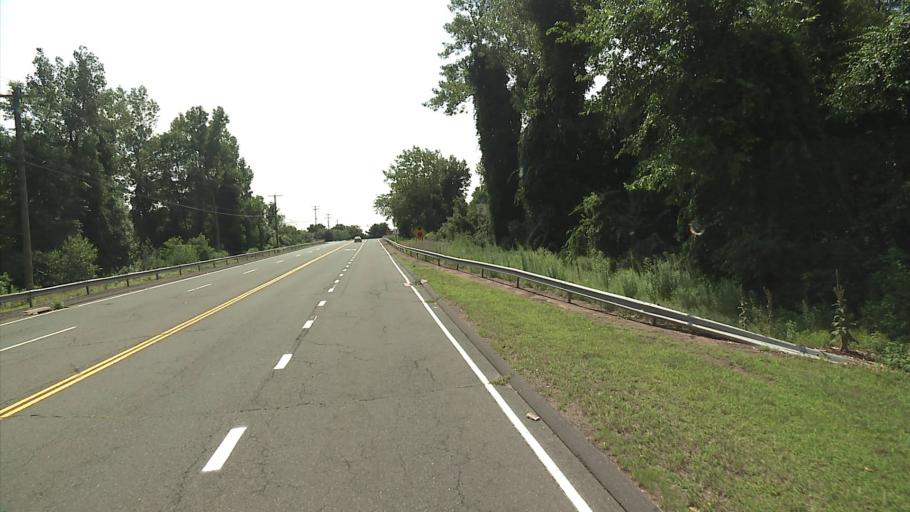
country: US
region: Connecticut
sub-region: Tolland County
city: Rockville
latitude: 41.8349
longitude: -72.4659
